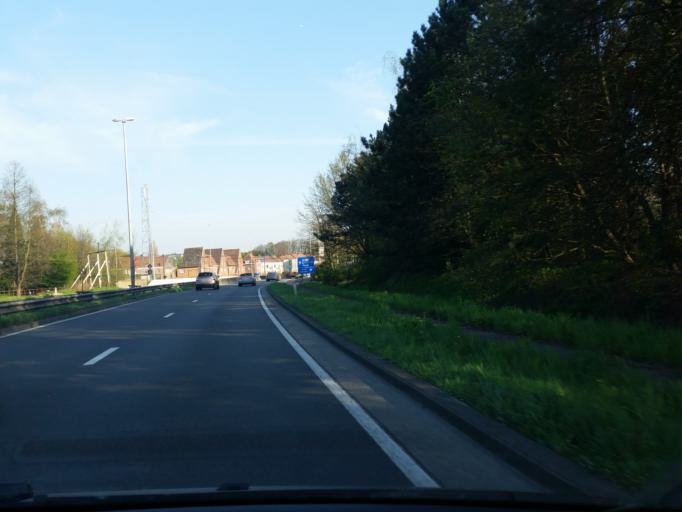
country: BE
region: Flanders
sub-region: Provincie Oost-Vlaanderen
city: Temse
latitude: 51.1321
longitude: 4.2175
